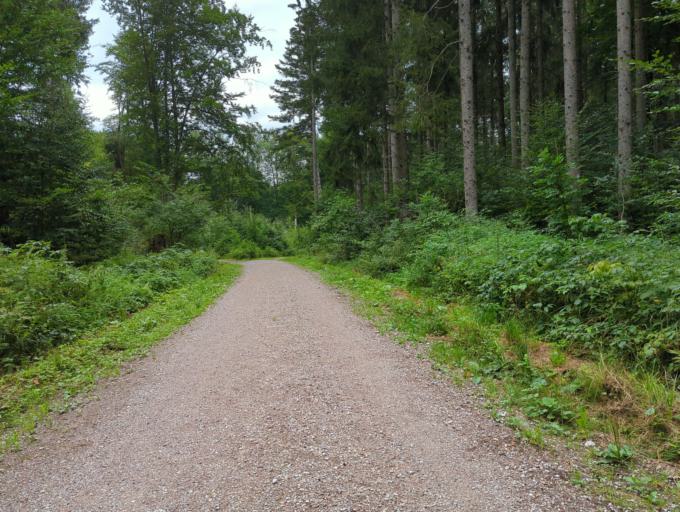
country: DE
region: Bavaria
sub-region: Swabia
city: Friesenried
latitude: 47.8650
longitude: 10.5448
